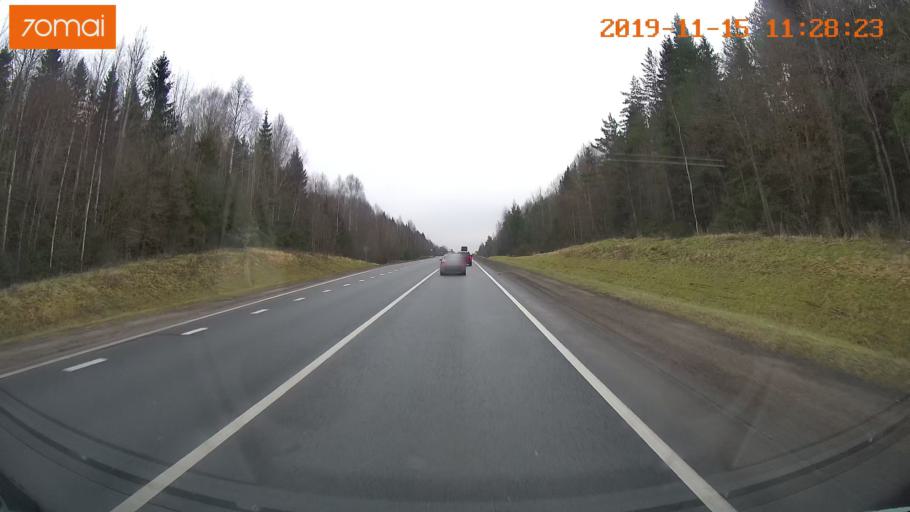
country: RU
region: Vologda
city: Molochnoye
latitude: 59.1723
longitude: 39.4870
